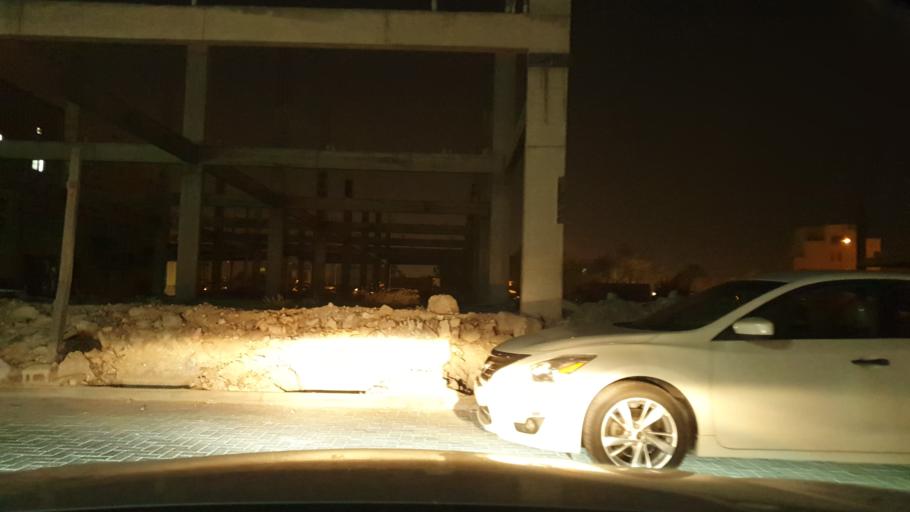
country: BH
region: Manama
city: Jidd Hafs
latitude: 26.1975
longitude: 50.4765
